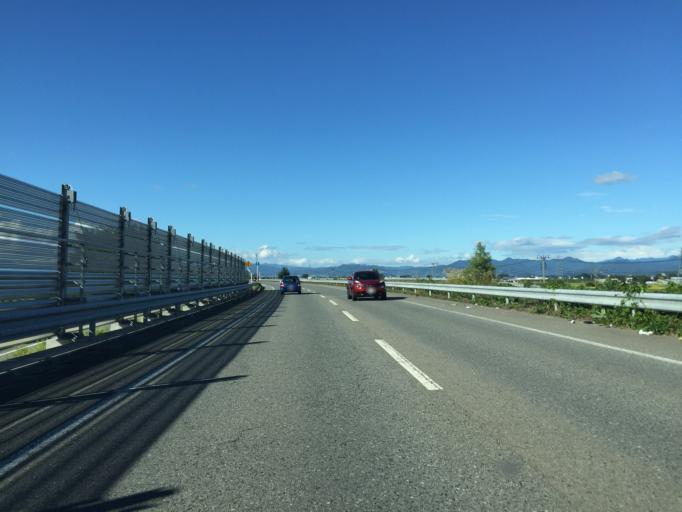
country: JP
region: Yamagata
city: Yonezawa
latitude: 37.9354
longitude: 140.1109
